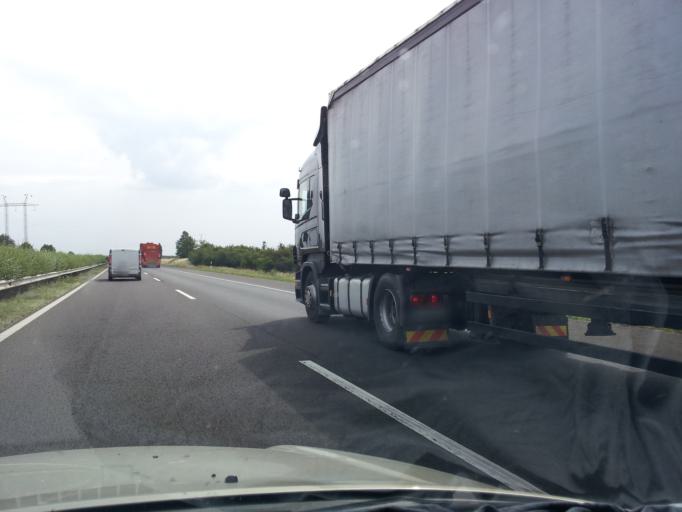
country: HU
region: Pest
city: Kartal
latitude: 47.6528
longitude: 19.5660
